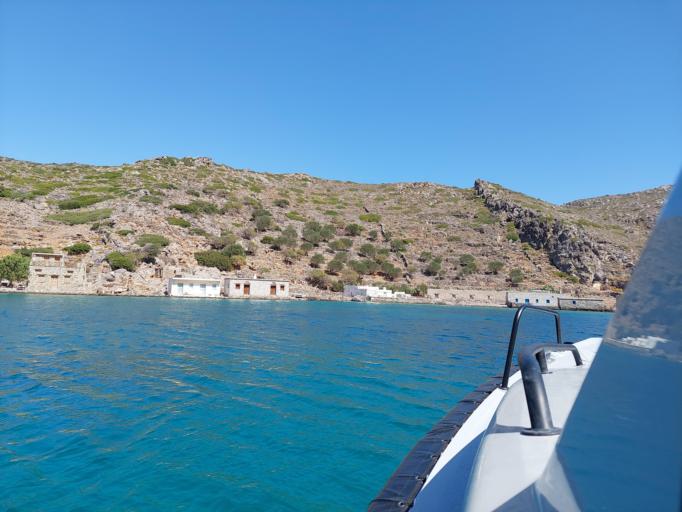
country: GR
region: South Aegean
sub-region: Nomos Dodekanisou
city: Karpathos
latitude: 35.8215
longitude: 27.2212
